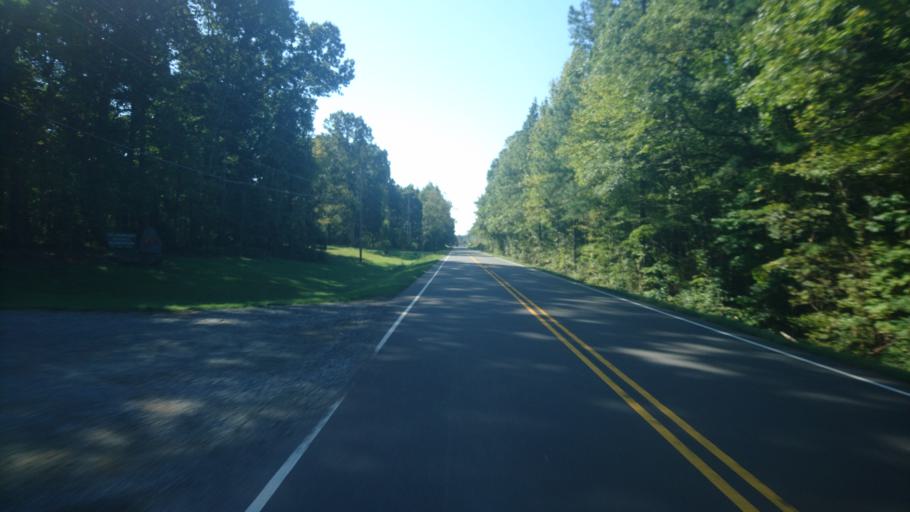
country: US
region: North Carolina
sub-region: Orange County
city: Hillsborough
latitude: 36.0343
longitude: -79.0814
